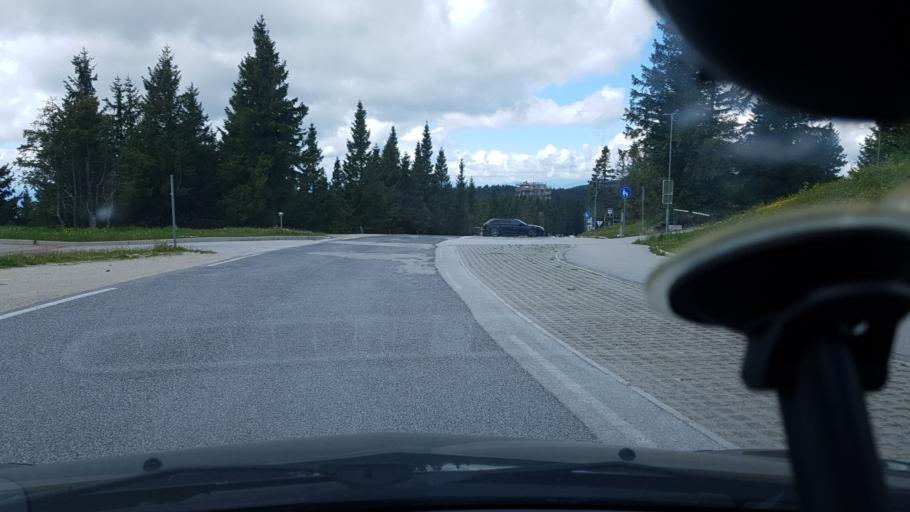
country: SI
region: Mislinja
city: Mislinja
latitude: 46.4527
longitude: 15.3317
